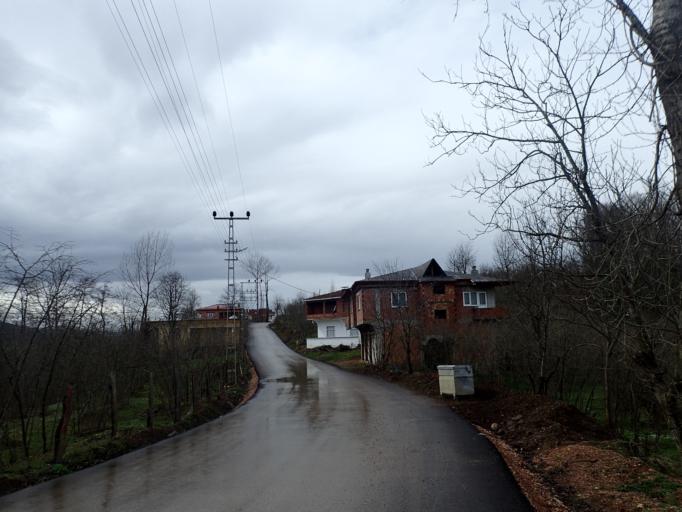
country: TR
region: Ordu
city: Camas
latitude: 40.8800
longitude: 37.5048
